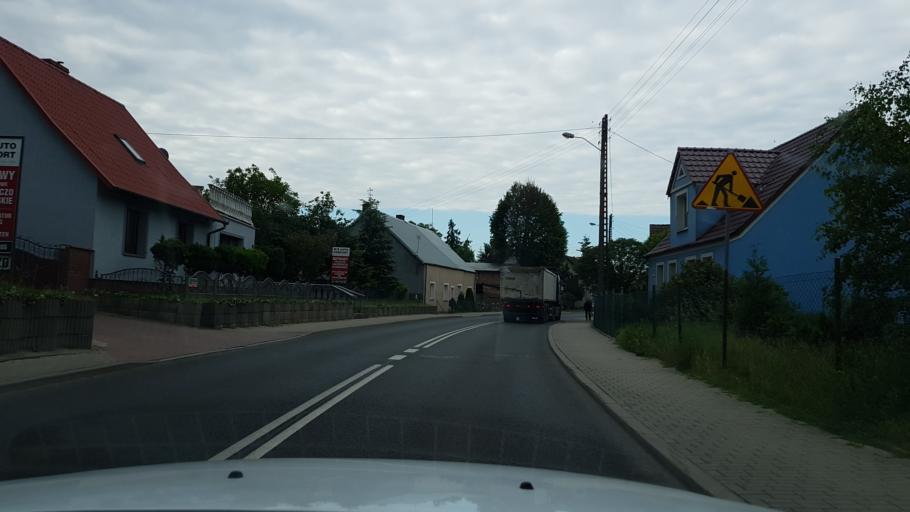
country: PL
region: West Pomeranian Voivodeship
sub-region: Powiat gryfinski
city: Gryfino
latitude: 53.2810
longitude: 14.5145
